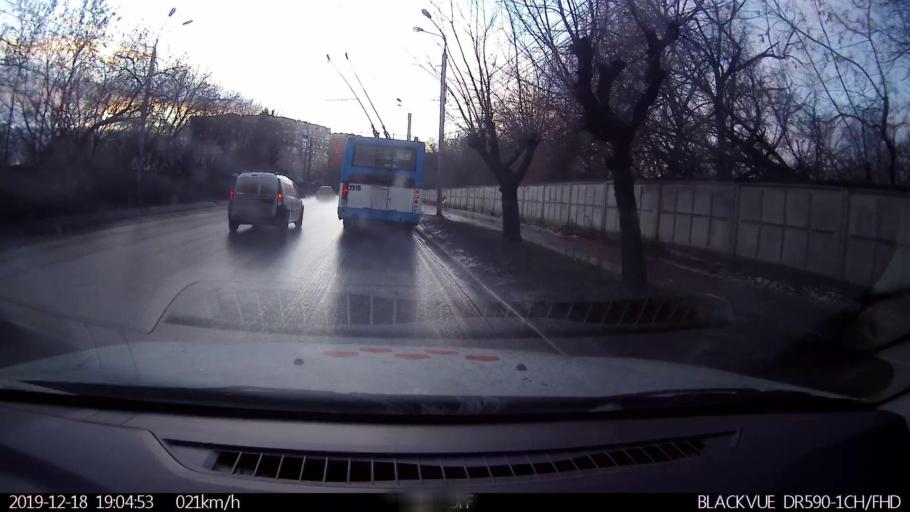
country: RU
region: Nizjnij Novgorod
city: Nizhniy Novgorod
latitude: 56.3299
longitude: 43.8678
